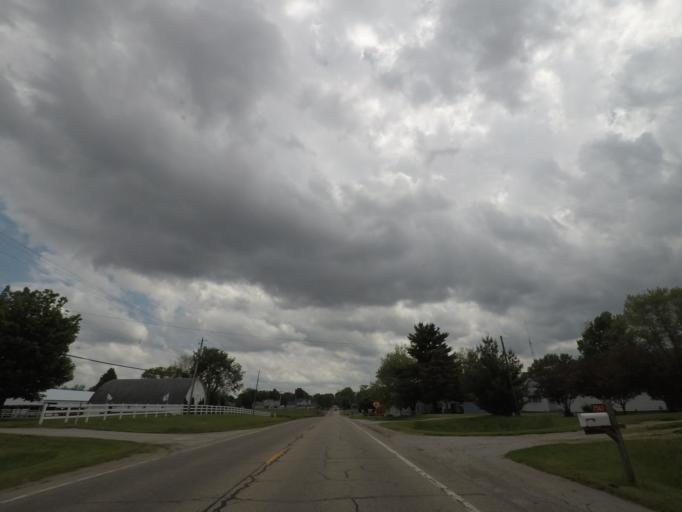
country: US
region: Illinois
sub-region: De Witt County
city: Clinton
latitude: 40.1632
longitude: -88.9605
